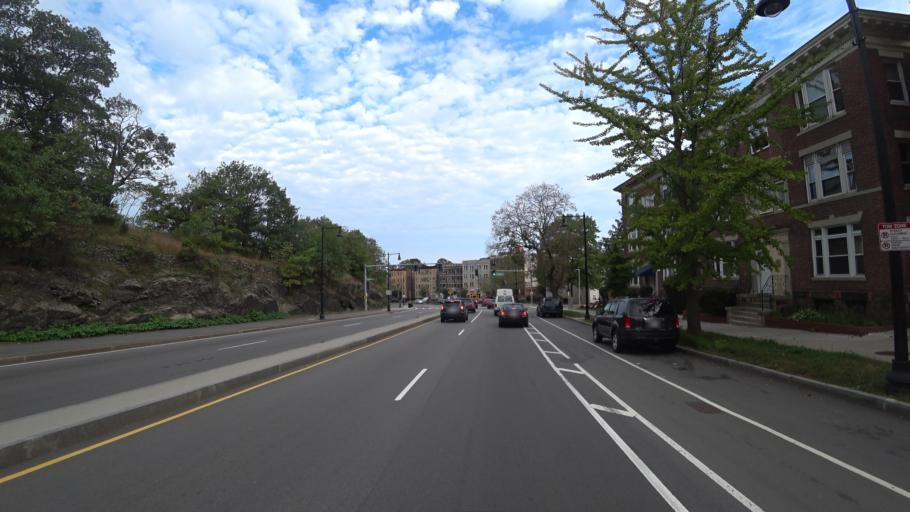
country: US
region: Massachusetts
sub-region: Suffolk County
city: Jamaica Plain
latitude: 42.3116
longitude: -71.0933
